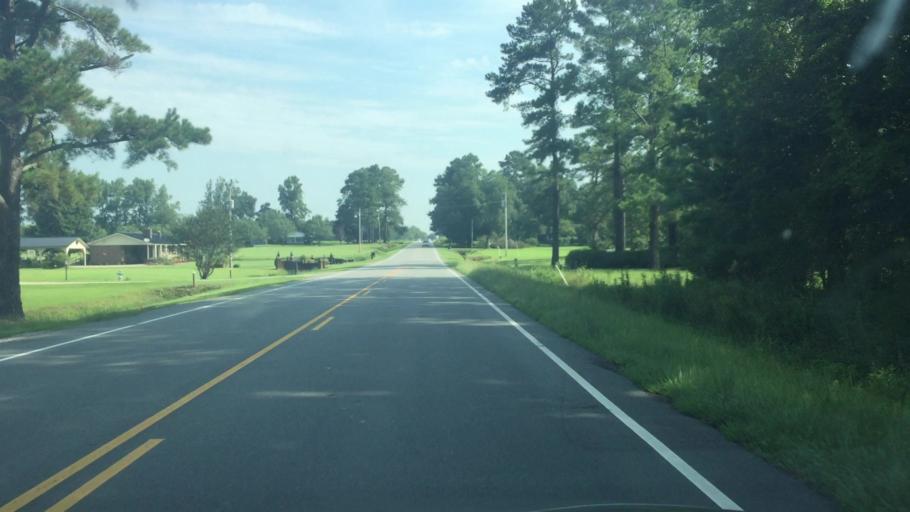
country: US
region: North Carolina
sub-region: Columbus County
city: Chadbourn
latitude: 34.2571
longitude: -78.8176
